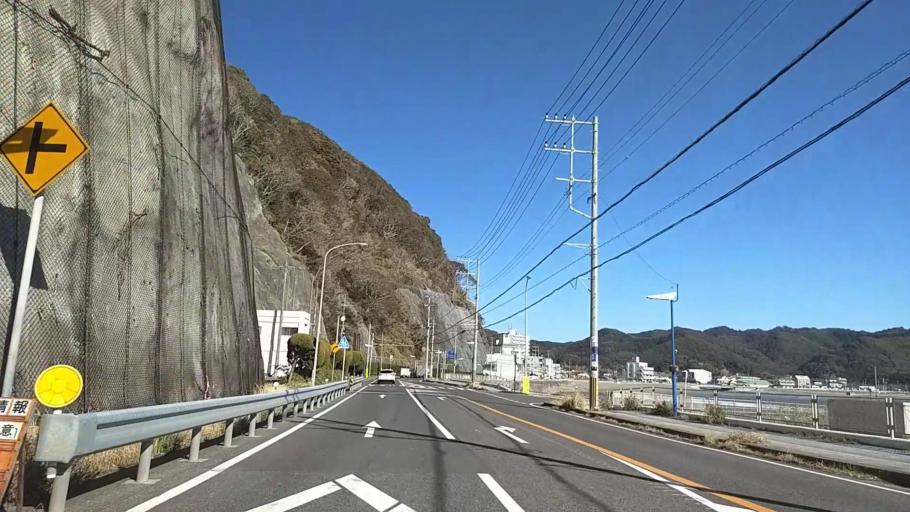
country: JP
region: Chiba
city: Kawaguchi
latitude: 35.1249
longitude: 140.1853
